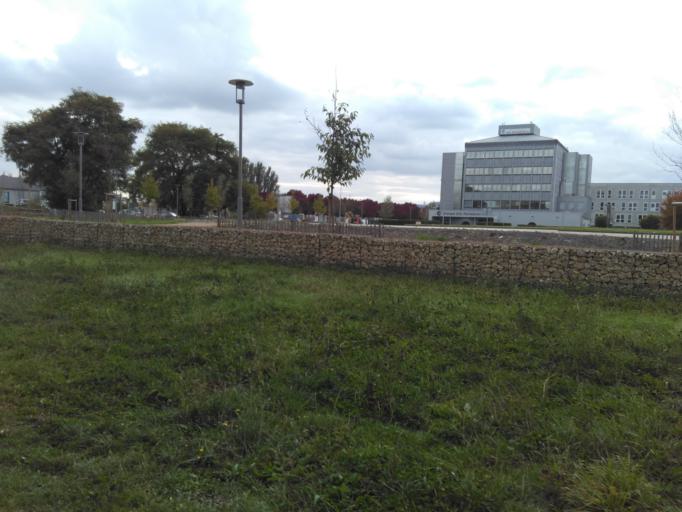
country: FR
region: Lorraine
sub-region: Departement de Meurthe-et-Moselle
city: Tomblaine
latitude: 48.6913
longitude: 6.2031
